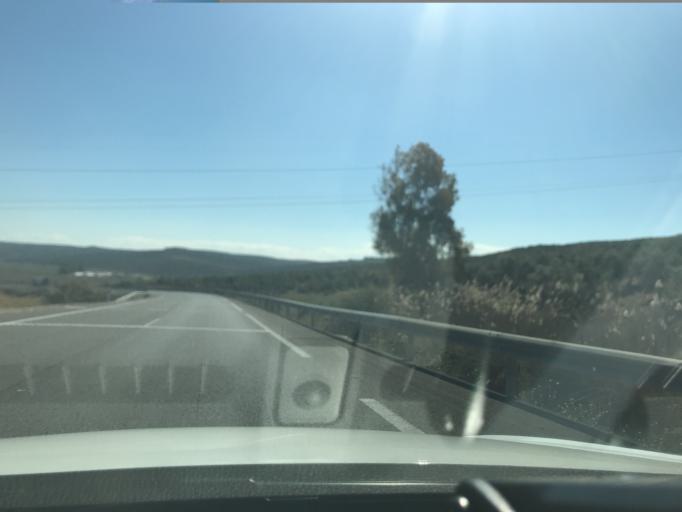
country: ES
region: Andalusia
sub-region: Provincia de Jaen
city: Marmolejo
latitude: 38.0047
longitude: -4.2071
